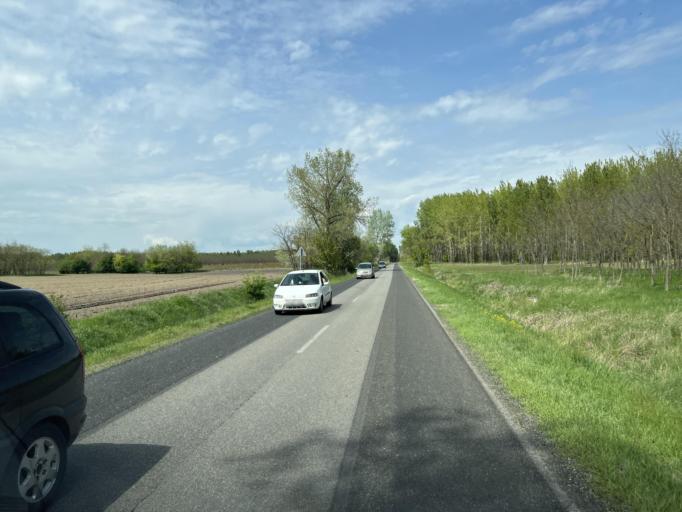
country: HU
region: Pest
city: Albertirsa
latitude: 47.1825
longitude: 19.6134
